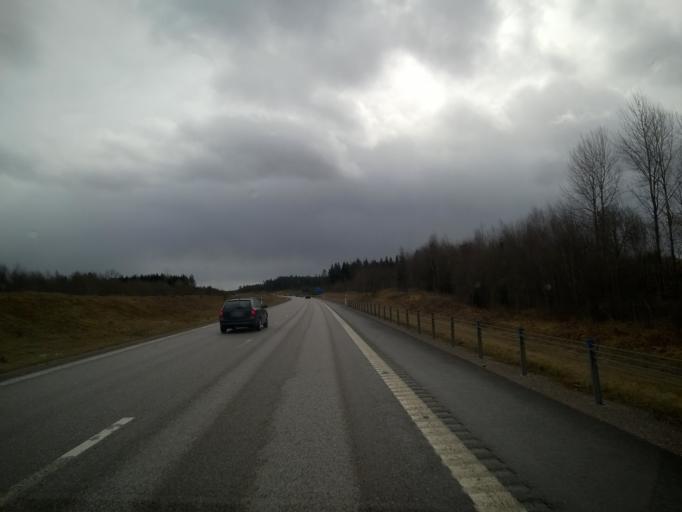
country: SE
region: Uppsala
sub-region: Osthammars Kommun
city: Bjorklinge
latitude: 60.0252
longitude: 17.6257
